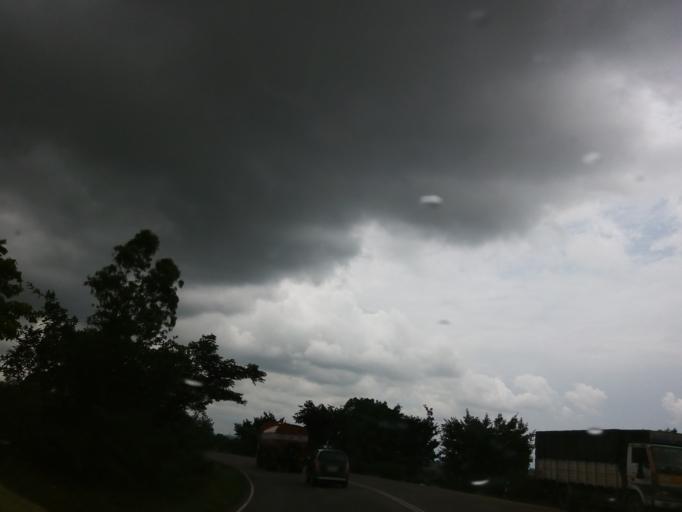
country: IN
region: Karnataka
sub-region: Hassan
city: Belur
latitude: 13.1633
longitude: 75.8994
